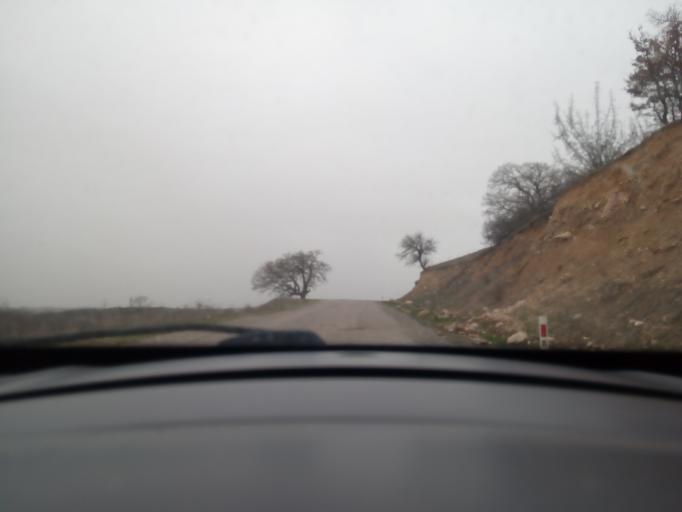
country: TR
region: Balikesir
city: Susurluk
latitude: 39.9150
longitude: 28.0985
